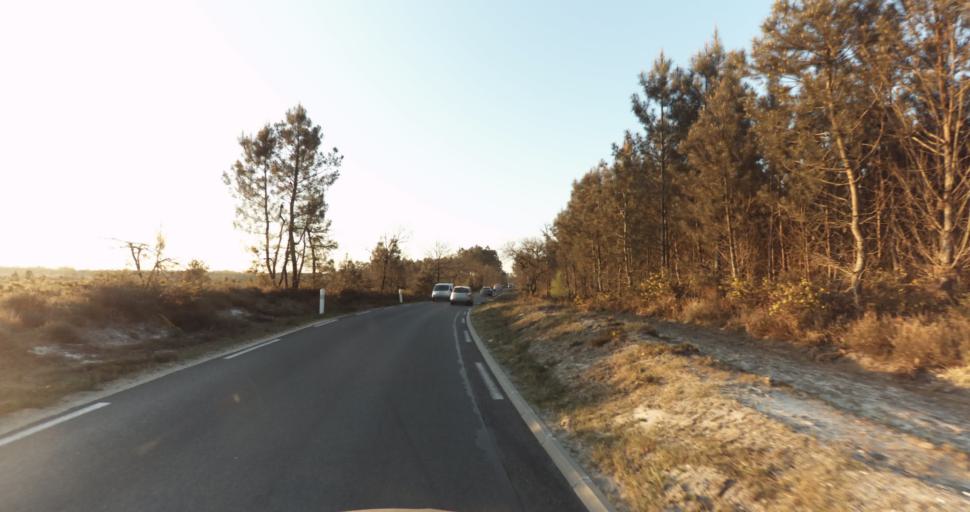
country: FR
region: Aquitaine
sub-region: Departement de la Gironde
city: Martignas-sur-Jalle
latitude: 44.8254
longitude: -0.7590
